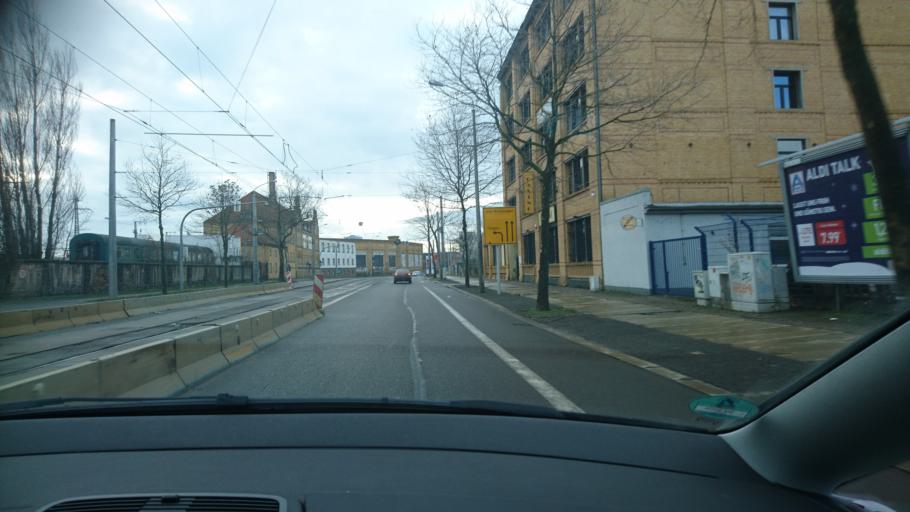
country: DE
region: Saxony
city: Leipzig
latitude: 51.3548
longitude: 12.3905
